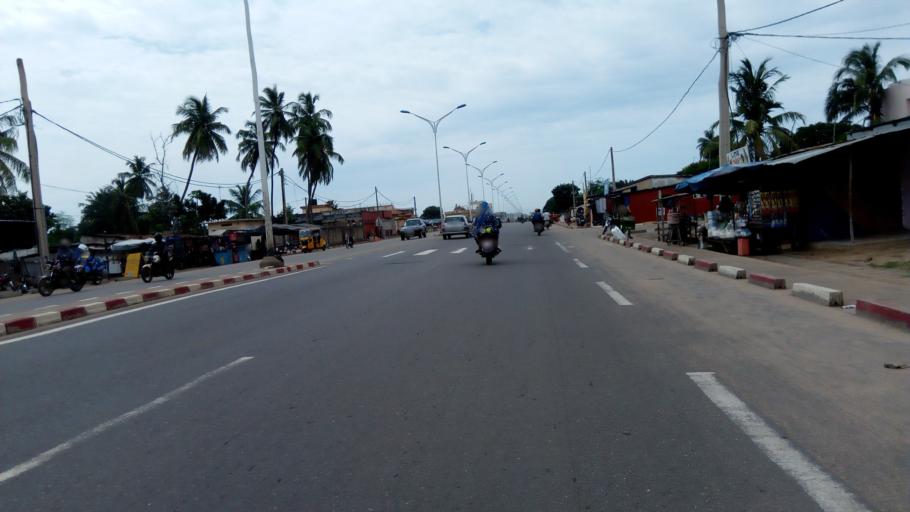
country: TG
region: Maritime
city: Lome
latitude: 6.1660
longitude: 1.2831
